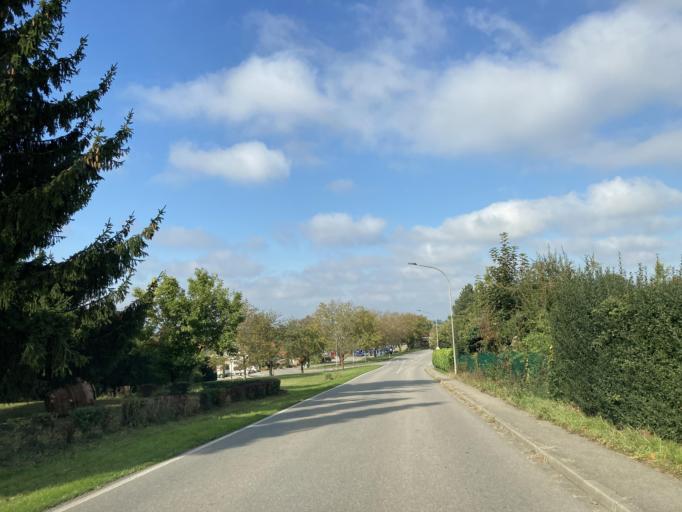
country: DE
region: Baden-Wuerttemberg
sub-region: Freiburg Region
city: Badenweiler
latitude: 47.8298
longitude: 7.6700
